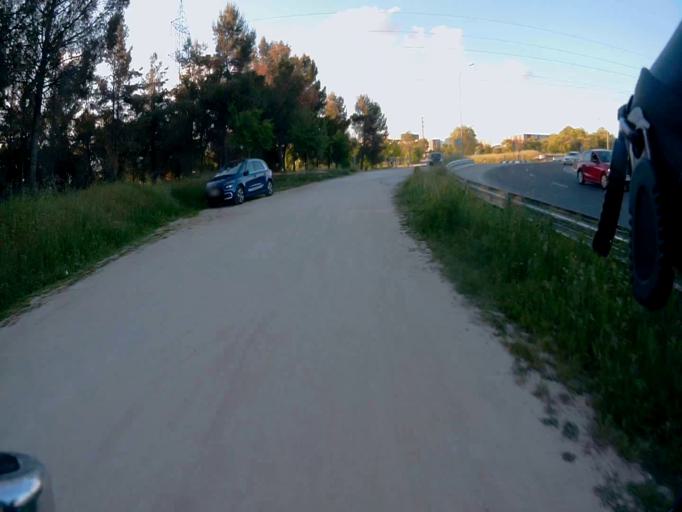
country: ES
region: Madrid
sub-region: Provincia de Madrid
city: Leganes
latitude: 40.3234
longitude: -3.7883
